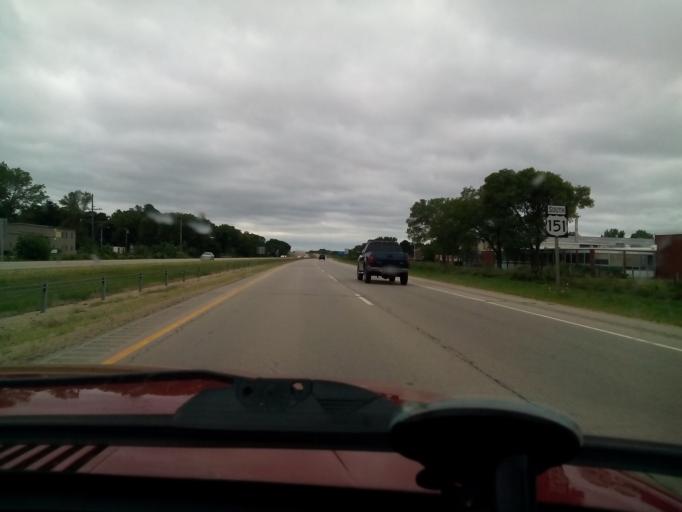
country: US
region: Wisconsin
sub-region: Dane County
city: Sun Prairie
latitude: 43.1835
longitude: -89.2387
